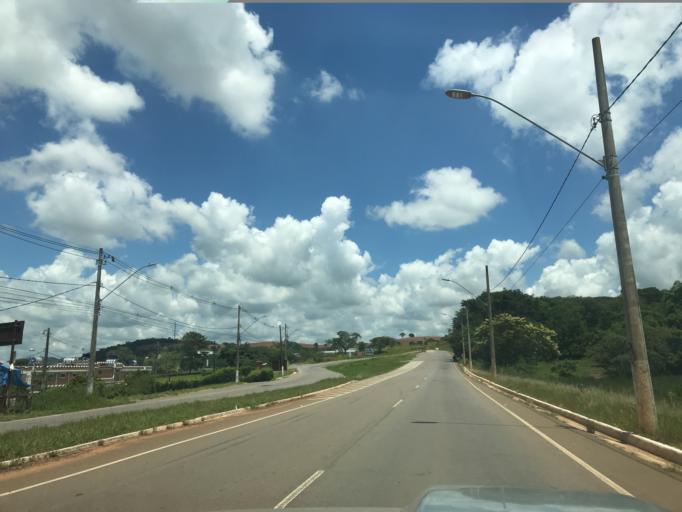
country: BR
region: Minas Gerais
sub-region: Tres Coracoes
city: Tres Coracoes
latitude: -21.6591
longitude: -45.2953
